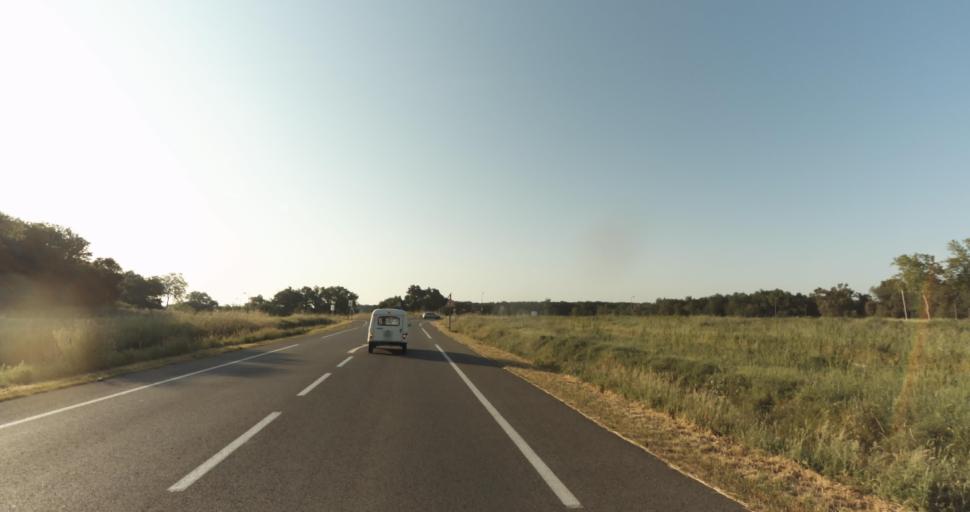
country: FR
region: Midi-Pyrenees
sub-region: Departement de la Haute-Garonne
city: Fonsorbes
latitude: 43.5265
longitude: 1.2039
